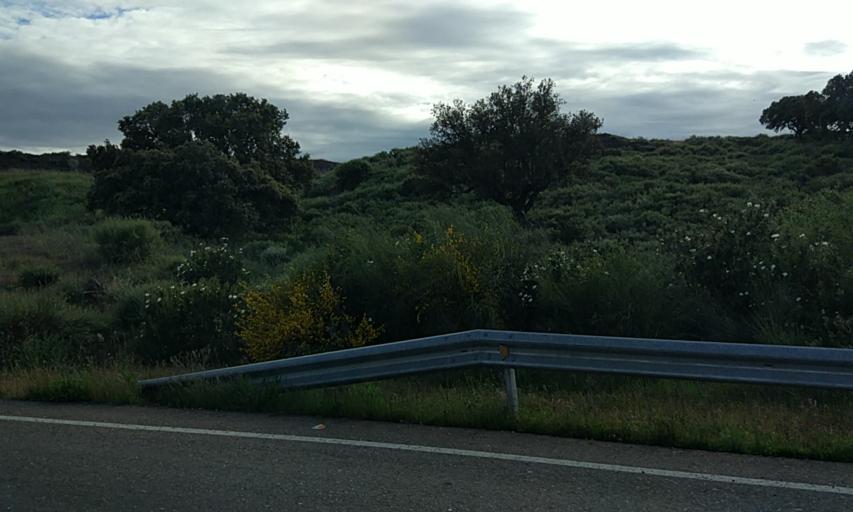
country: ES
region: Extremadura
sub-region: Provincia de Caceres
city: Casas de Don Gomez
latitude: 40.0293
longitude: -6.6111
